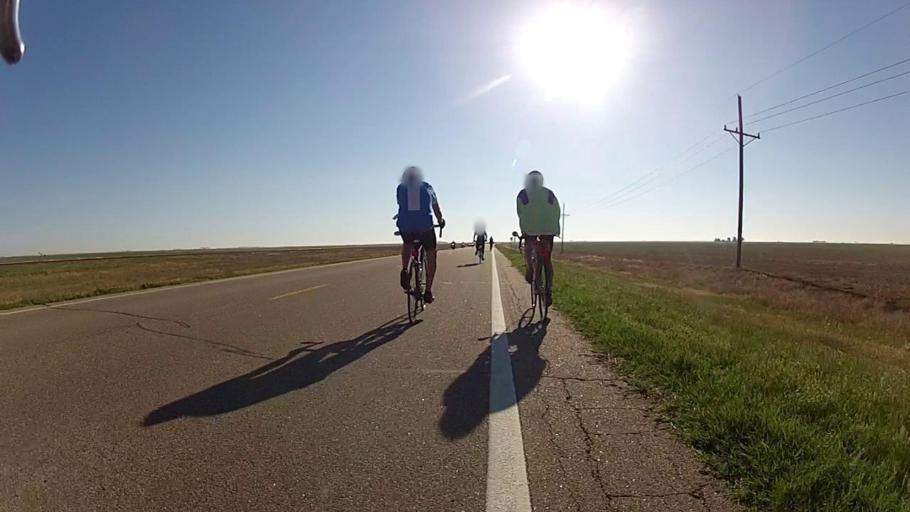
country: US
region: Kansas
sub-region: Haskell County
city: Sublette
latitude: 37.5168
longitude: -100.7237
